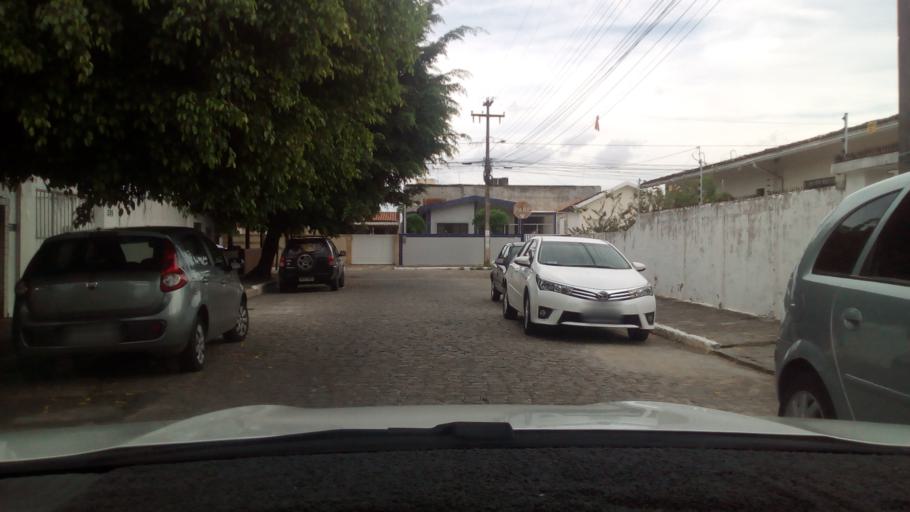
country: BR
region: Paraiba
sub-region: Joao Pessoa
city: Joao Pessoa
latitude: -7.1235
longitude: -34.8543
